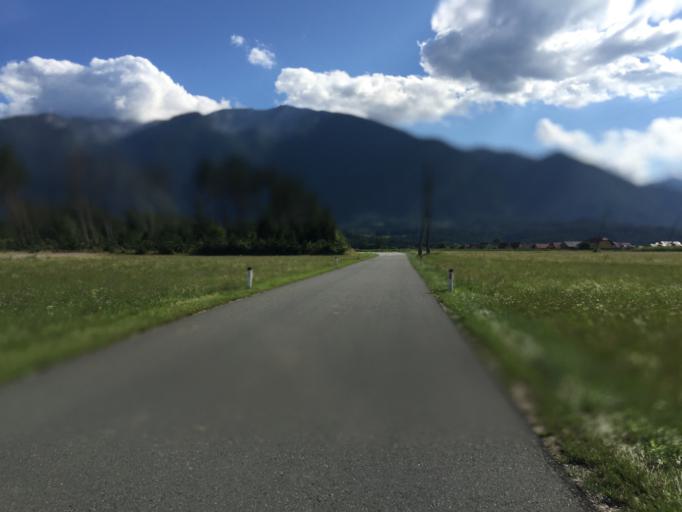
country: AT
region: Carinthia
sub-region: Politischer Bezirk Volkermarkt
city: Feistritz ob Bleiburg
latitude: 46.5659
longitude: 14.7683
